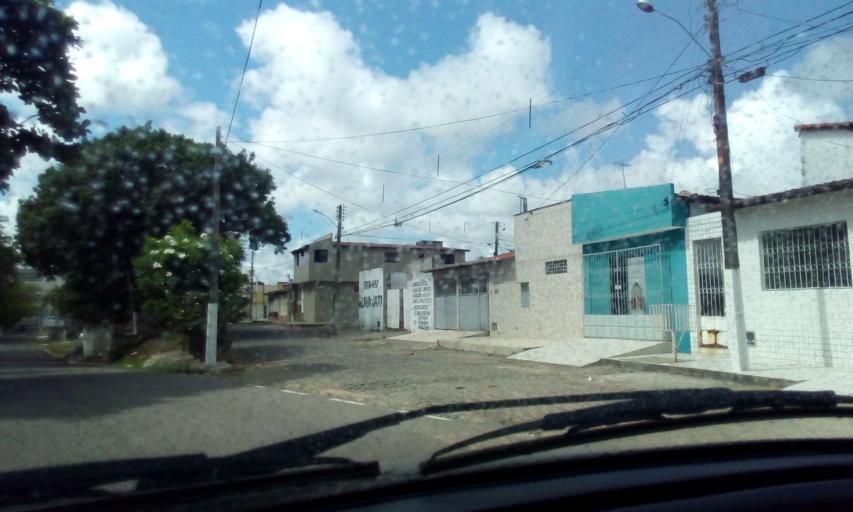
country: BR
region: Rio Grande do Norte
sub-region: Natal
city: Natal
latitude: -5.8669
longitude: -35.2075
